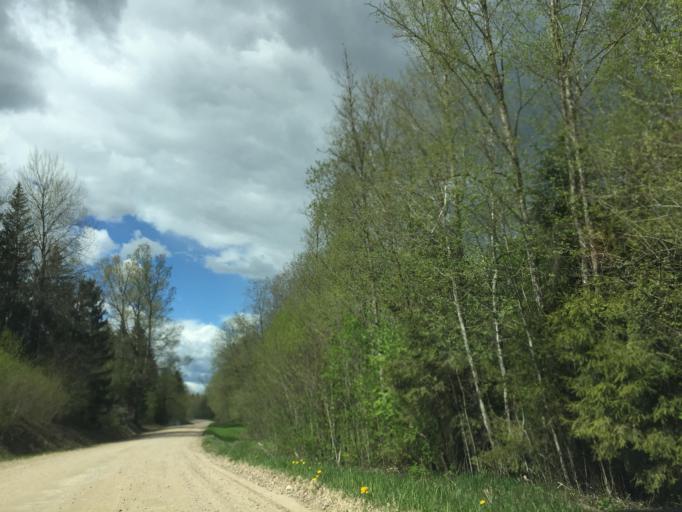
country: LV
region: Madonas Rajons
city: Madona
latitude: 56.9247
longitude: 26.0204
